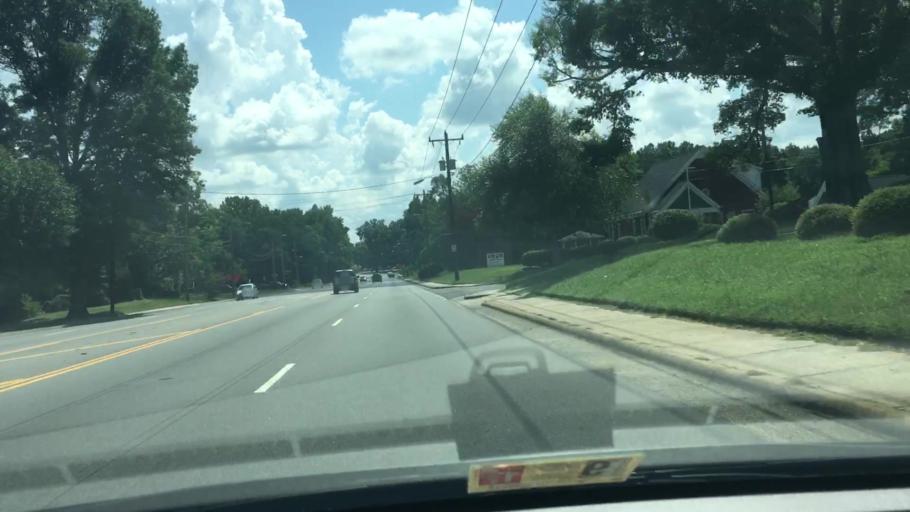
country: US
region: North Carolina
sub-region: Mecklenburg County
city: Charlotte
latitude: 35.2639
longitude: -80.7952
